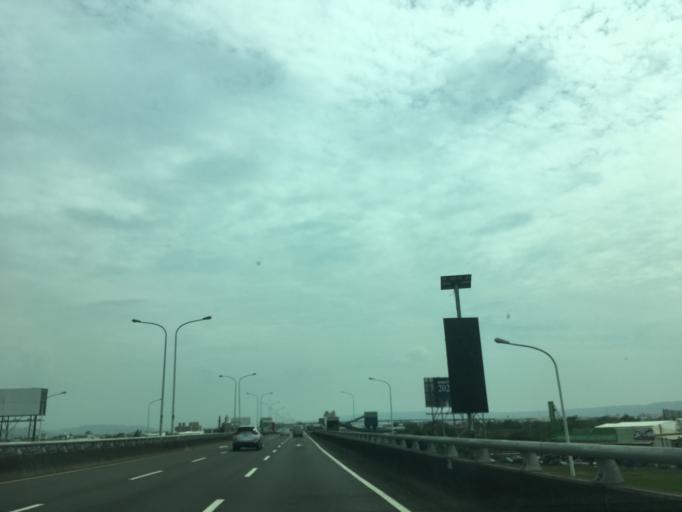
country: TW
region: Taiwan
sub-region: Taichung City
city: Taichung
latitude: 24.0857
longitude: 120.6642
